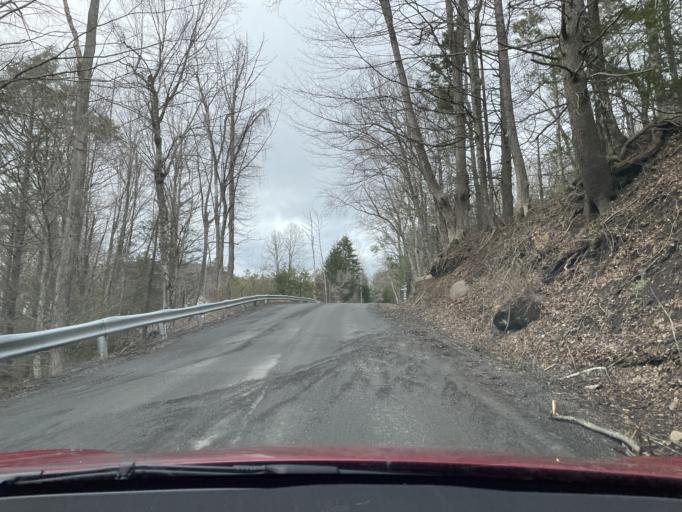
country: US
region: New York
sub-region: Ulster County
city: Woodstock
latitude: 42.0716
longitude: -74.1547
